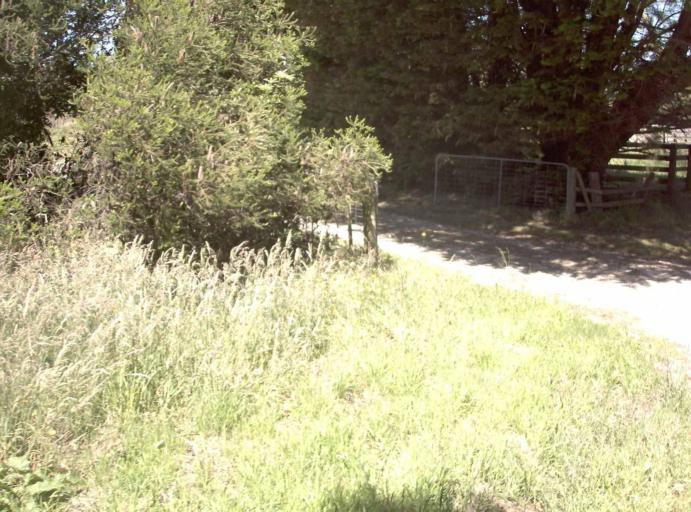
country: AU
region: Victoria
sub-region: Bass Coast
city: North Wonthaggi
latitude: -38.7754
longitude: 146.0741
